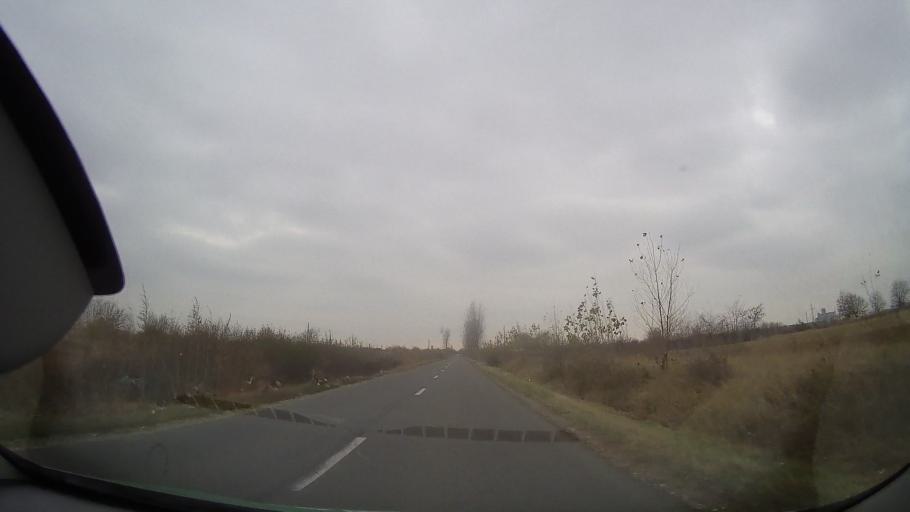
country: RO
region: Ialomita
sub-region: Comuna Manasia
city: Manasia
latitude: 44.7174
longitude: 26.6827
